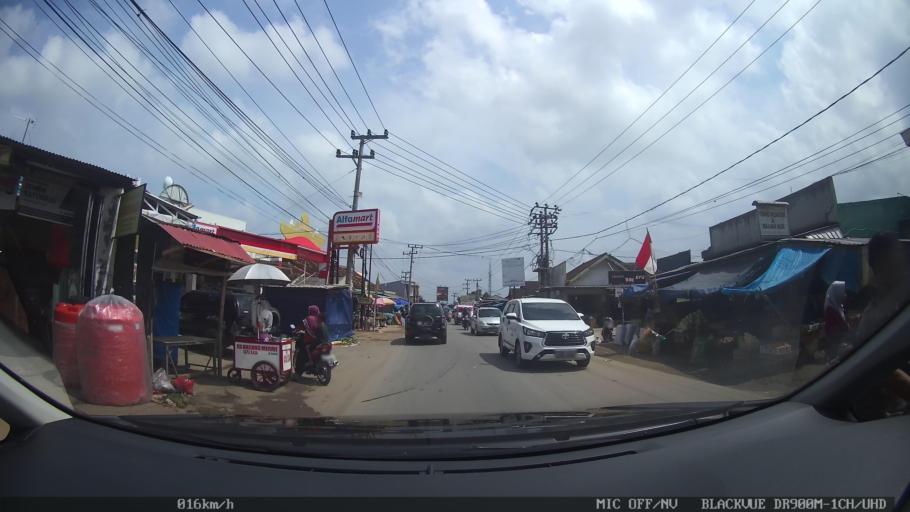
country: ID
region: Lampung
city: Kedaton
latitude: -5.3390
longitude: 105.2932
